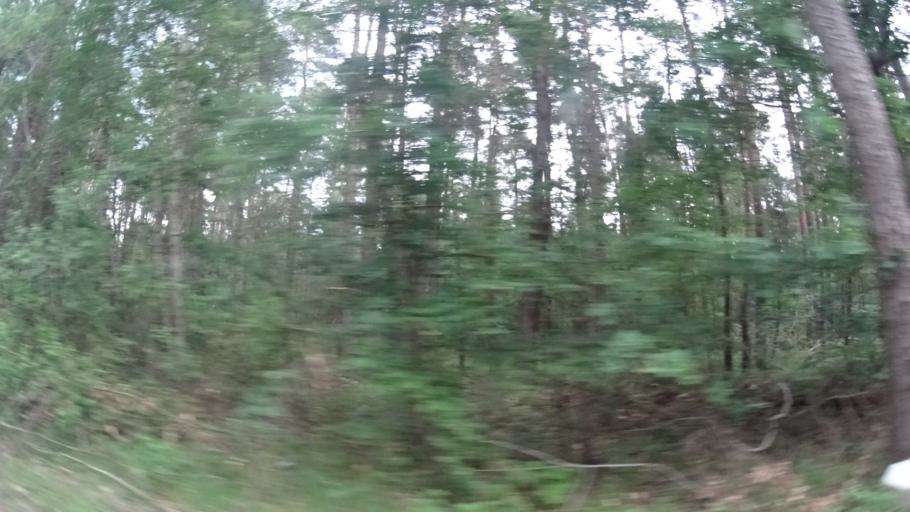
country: DE
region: Rheinland-Pfalz
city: Dudenhofen
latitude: 49.3345
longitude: 8.3737
